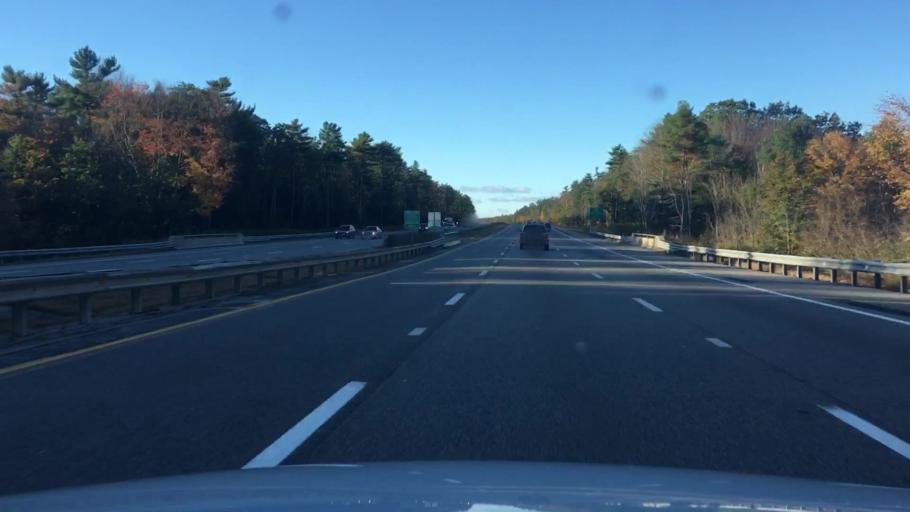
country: US
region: Maine
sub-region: York County
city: West Kennebunk
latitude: 43.4304
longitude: -70.5473
